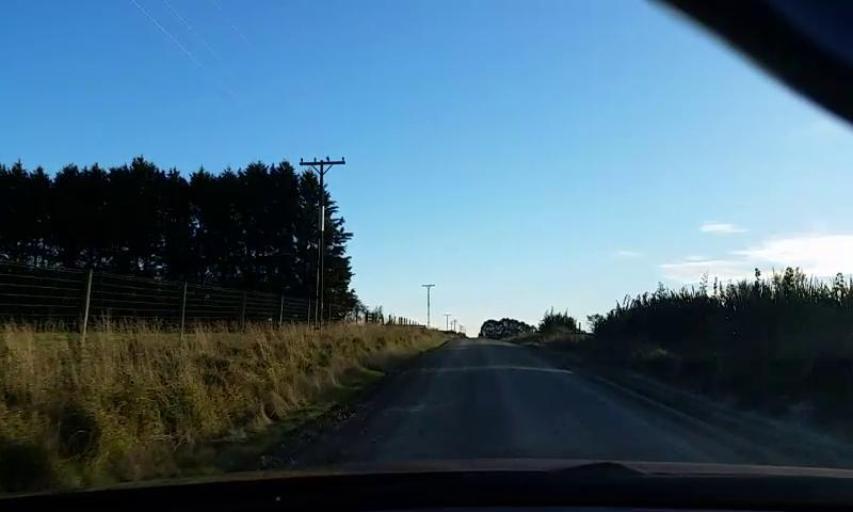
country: NZ
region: Southland
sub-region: Invercargill City
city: Invercargill
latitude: -46.2851
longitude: 168.4831
